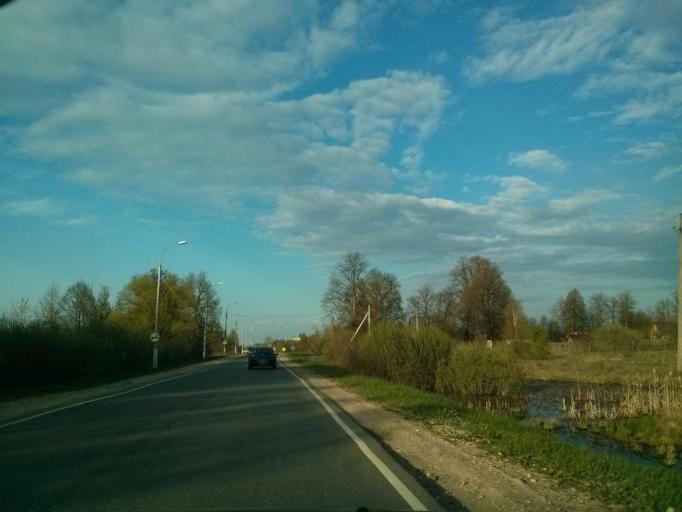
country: RU
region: Nizjnij Novgorod
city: Navashino
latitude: 55.6048
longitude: 42.1946
